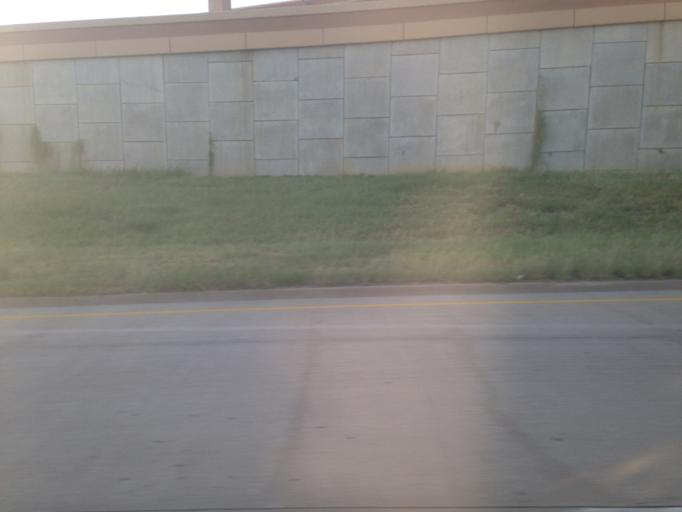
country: US
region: Texas
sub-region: Tarrant County
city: North Richland Hills
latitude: 32.8323
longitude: -97.2021
